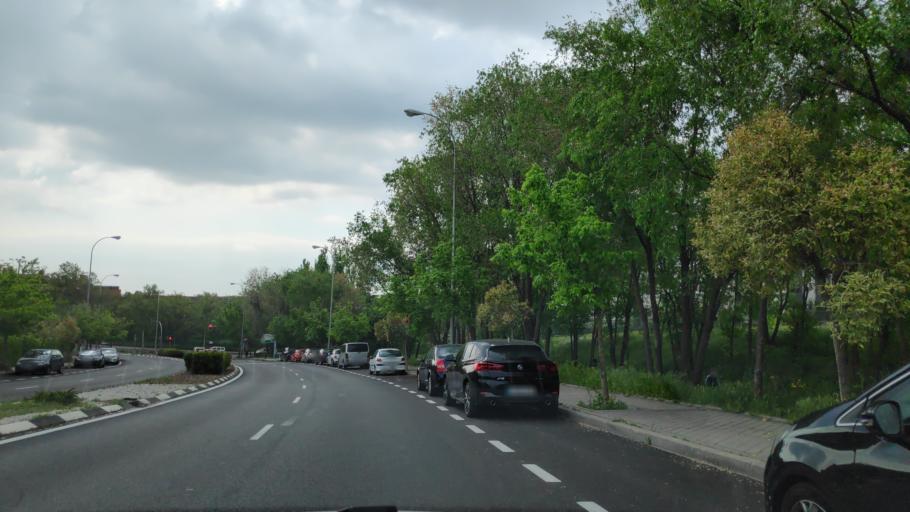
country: ES
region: Madrid
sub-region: Provincia de Madrid
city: Pozuelo de Alarcon
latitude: 40.4566
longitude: -3.7865
